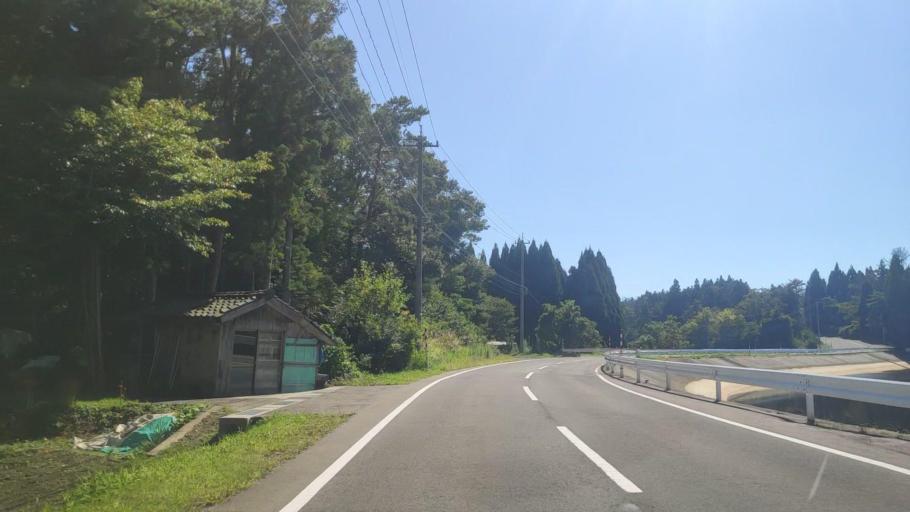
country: JP
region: Ishikawa
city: Nanao
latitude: 37.4752
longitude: 137.3342
